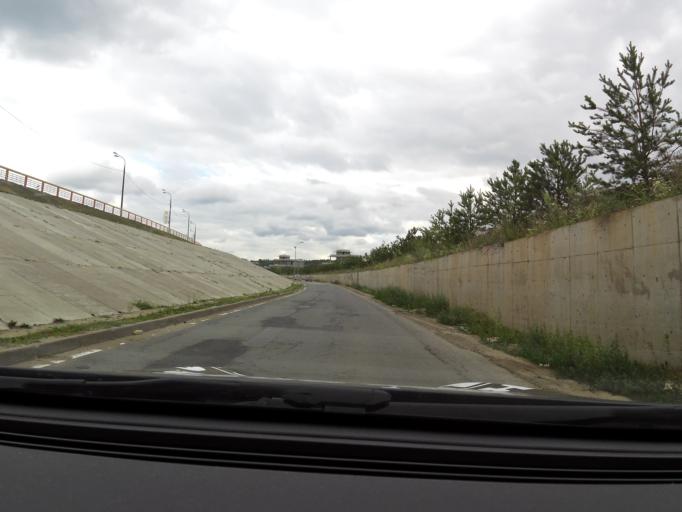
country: RU
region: Tatarstan
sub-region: Gorod Kazan'
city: Kazan
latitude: 55.8096
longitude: 49.1346
